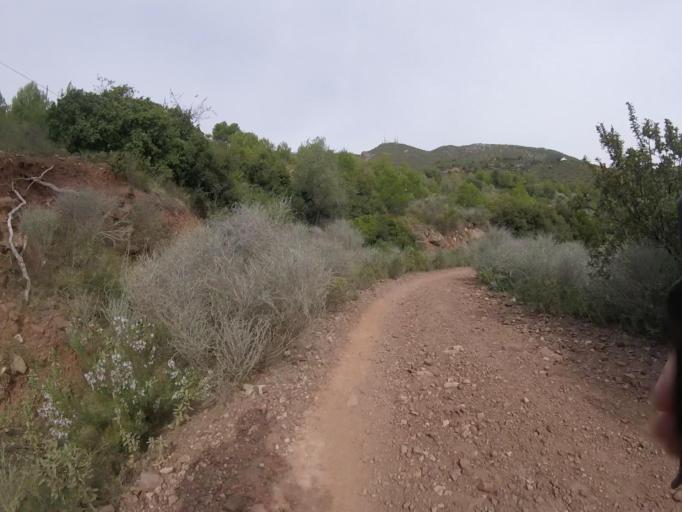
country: ES
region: Valencia
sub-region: Provincia de Castello
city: Benicassim
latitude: 40.0711
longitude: 0.0355
